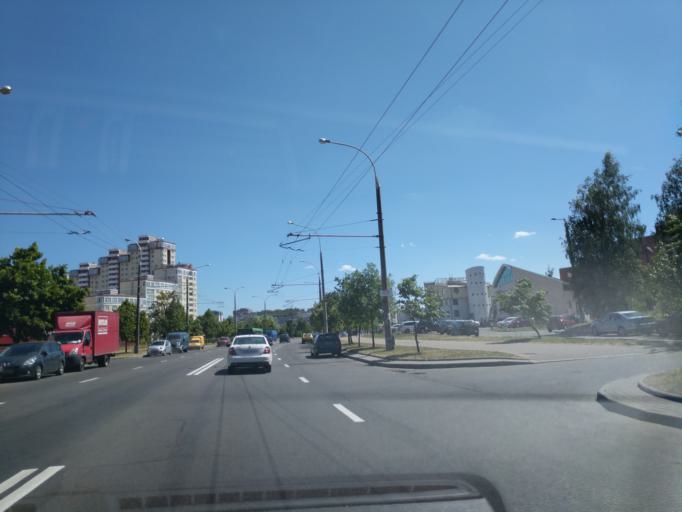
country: BY
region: Minsk
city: Borovlyany
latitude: 53.9497
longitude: 27.6774
